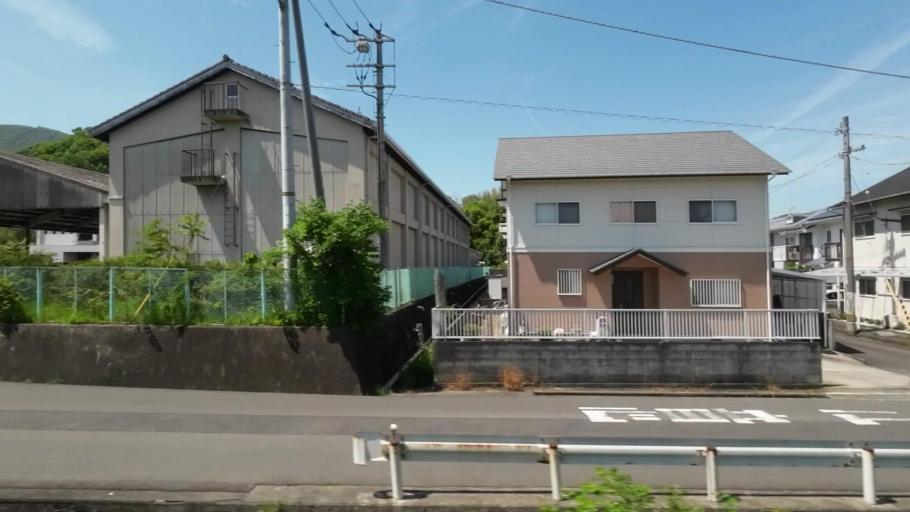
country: JP
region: Kagawa
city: Marugame
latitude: 34.2228
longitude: 133.7938
